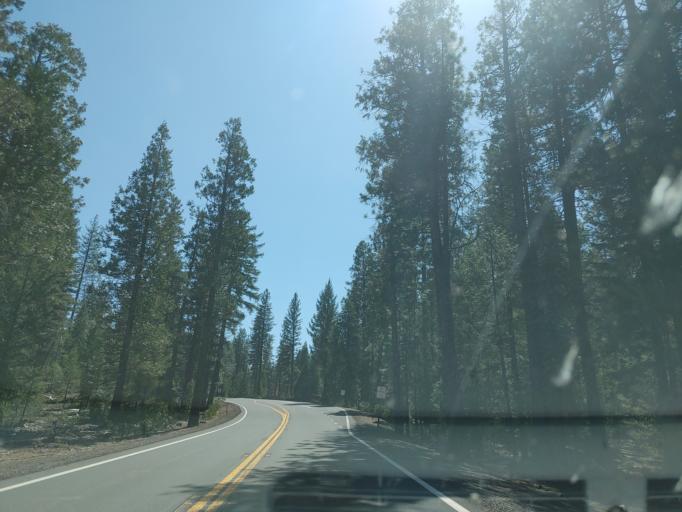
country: US
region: California
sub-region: Shasta County
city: Burney
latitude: 41.0124
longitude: -121.6492
